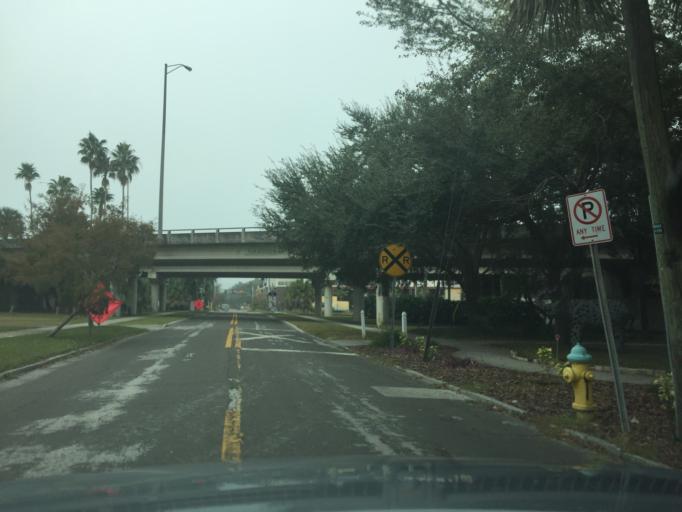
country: US
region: Florida
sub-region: Hillsborough County
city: Tampa
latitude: 27.9337
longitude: -82.4810
